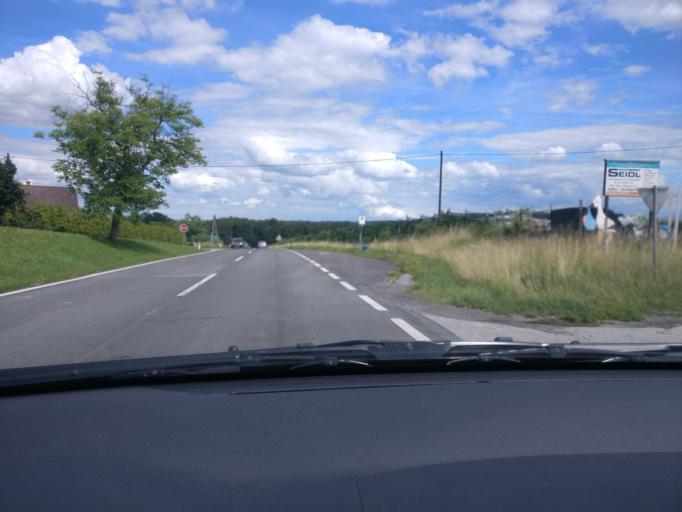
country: AT
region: Styria
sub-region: Politischer Bezirk Hartberg-Fuerstenfeld
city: Dienersdorf
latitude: 47.2133
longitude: 15.8629
